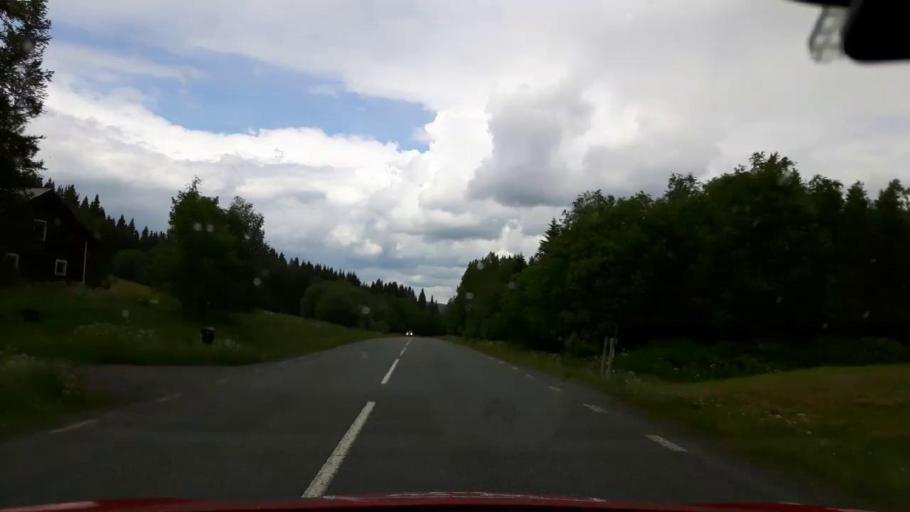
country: SE
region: Jaemtland
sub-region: Krokoms Kommun
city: Krokom
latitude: 63.4968
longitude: 14.2137
